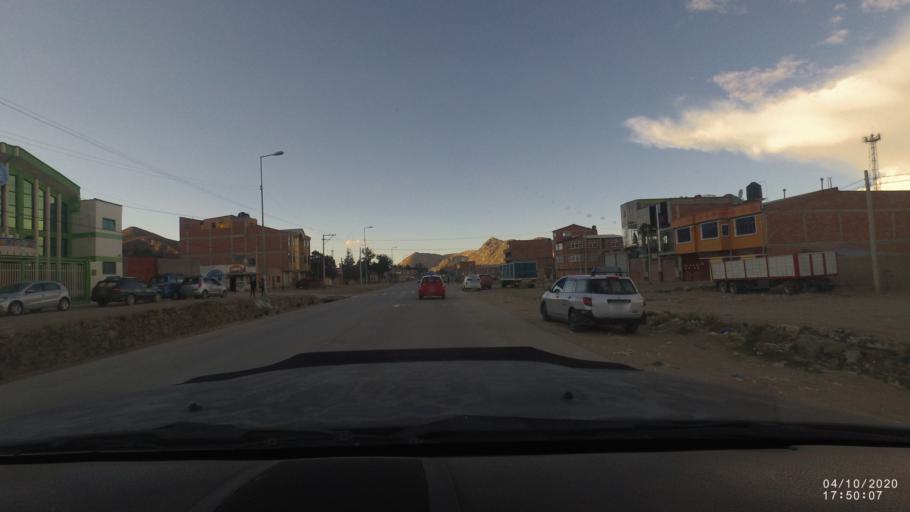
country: BO
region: Oruro
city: Oruro
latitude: -18.0040
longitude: -67.1359
